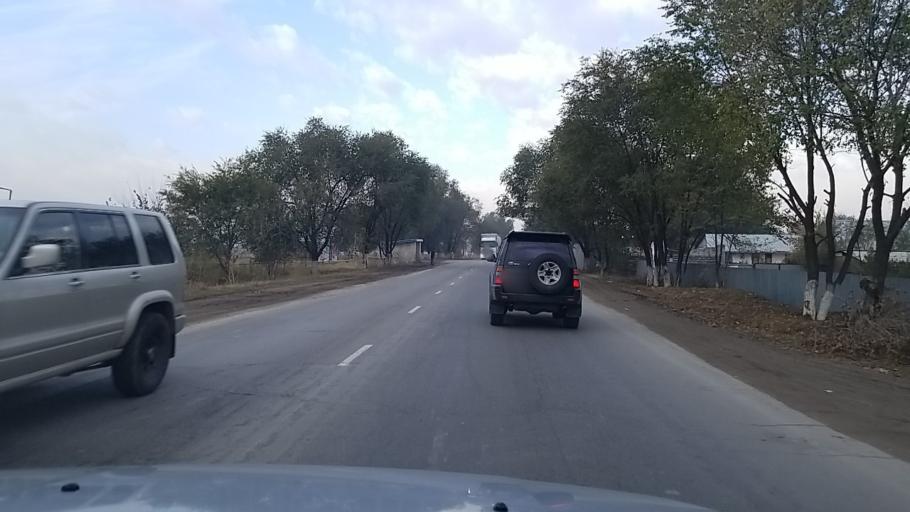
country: KZ
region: Almaty Oblysy
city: Burunday
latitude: 43.3590
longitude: 76.7559
